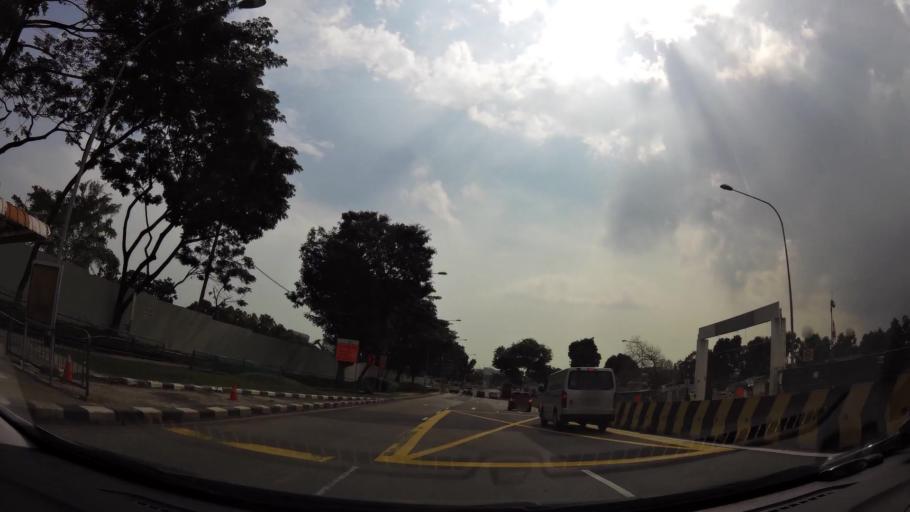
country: SG
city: Singapore
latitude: 1.3395
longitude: 103.9610
